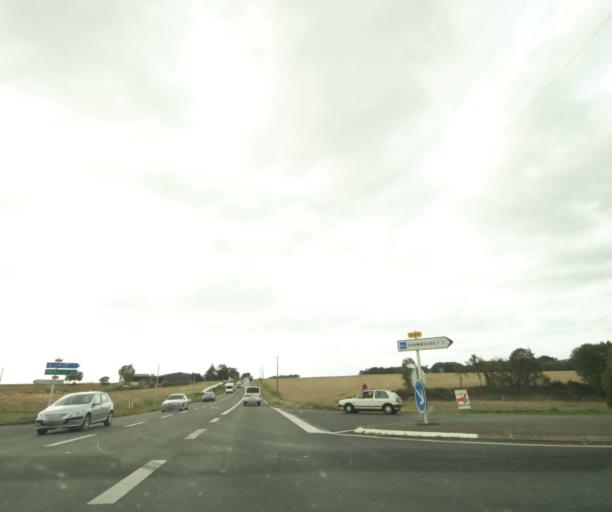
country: FR
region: Centre
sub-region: Departement d'Indre-et-Loire
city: Chambourg-sur-Indre
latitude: 47.1813
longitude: 0.9593
